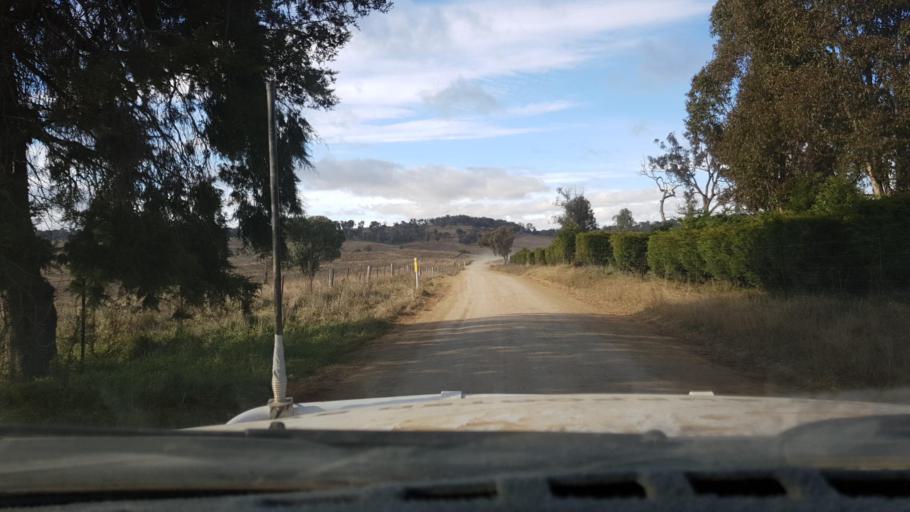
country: AU
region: New South Wales
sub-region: Armidale Dumaresq
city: Enmore
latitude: -30.7673
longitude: 151.6372
